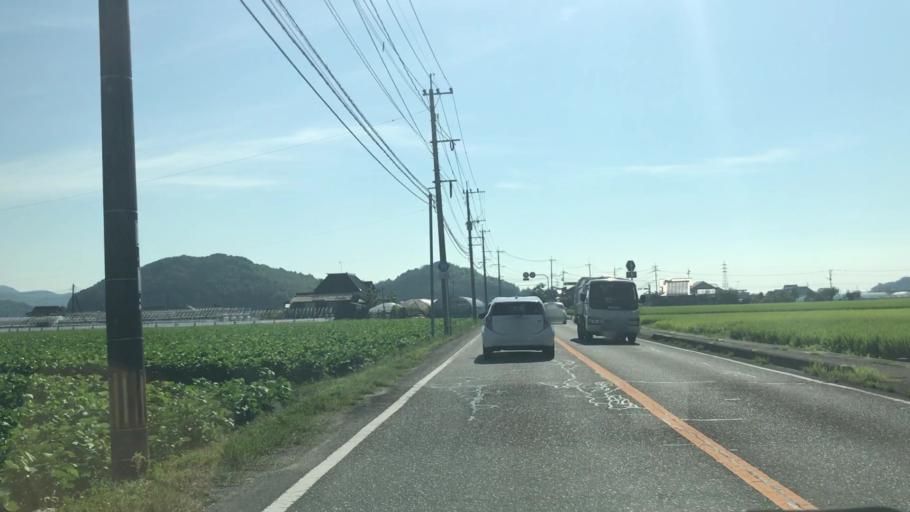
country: JP
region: Saga Prefecture
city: Takeocho-takeo
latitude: 33.2089
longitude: 130.0732
